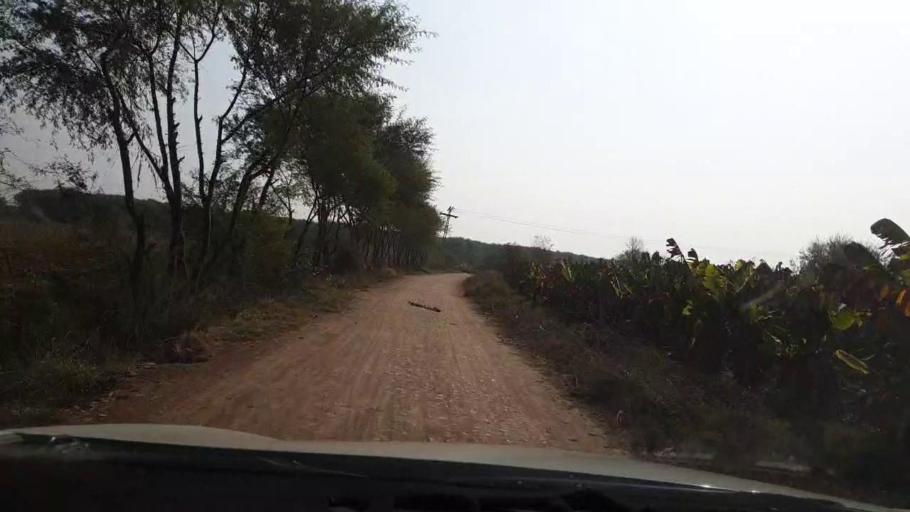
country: PK
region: Sindh
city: Matiari
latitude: 25.6234
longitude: 68.4976
